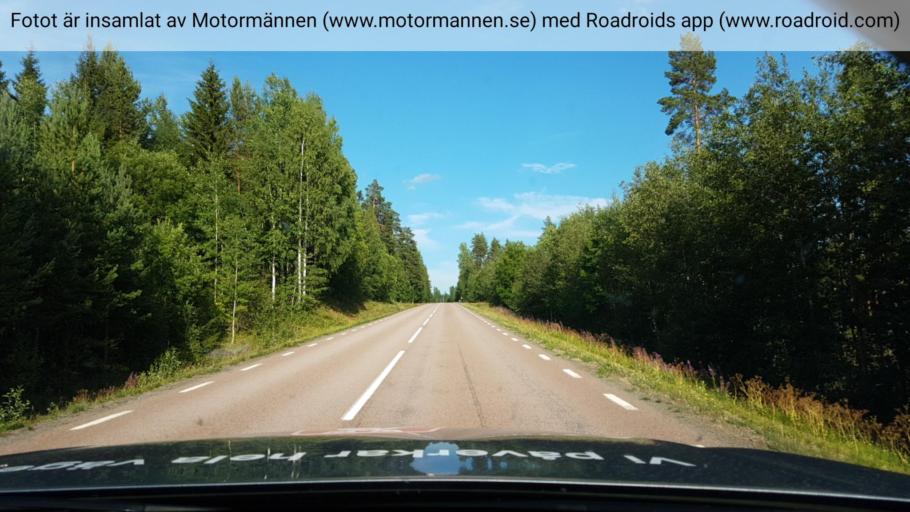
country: SE
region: Vaesternorrland
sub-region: Solleftea Kommun
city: As
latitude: 63.5956
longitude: 16.2383
